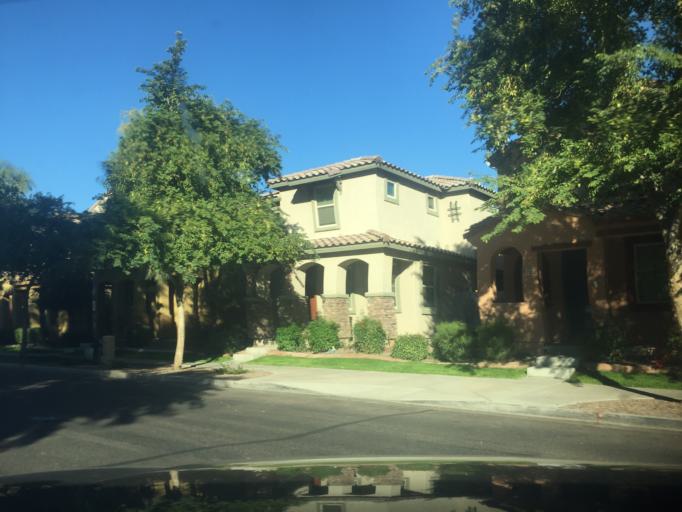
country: US
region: Arizona
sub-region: Maricopa County
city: Tolleson
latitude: 33.4712
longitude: -112.2264
